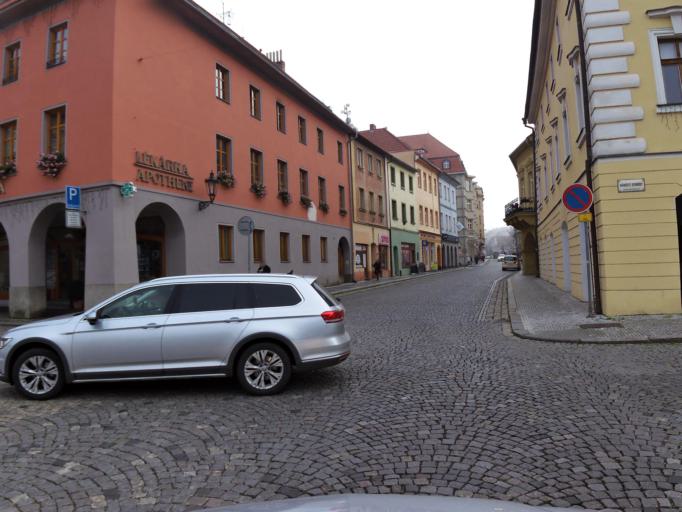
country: CZ
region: Ustecky
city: Zatec
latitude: 50.3285
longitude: 13.5449
